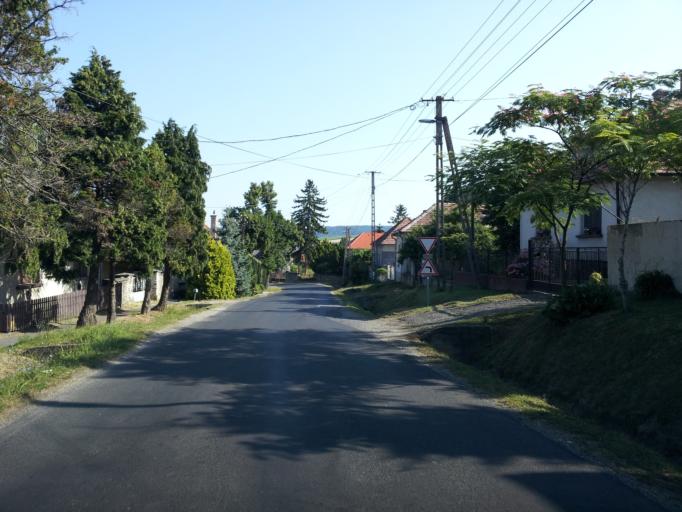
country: HU
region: Zala
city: Gyenesdias
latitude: 46.8639
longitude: 17.2977
